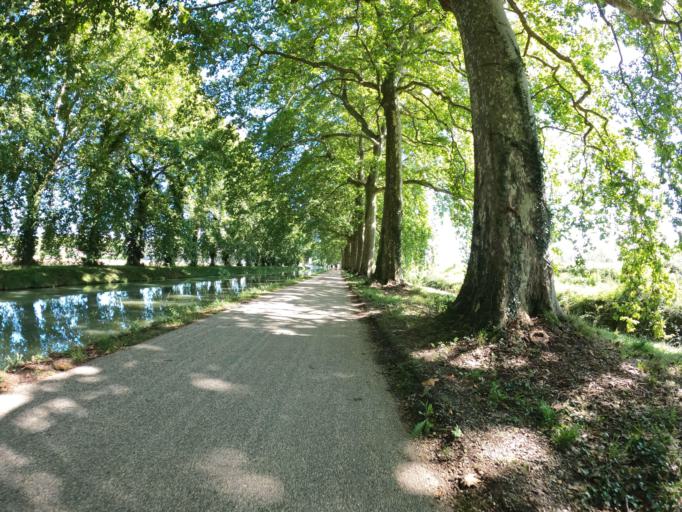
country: FR
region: Midi-Pyrenees
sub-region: Departement du Tarn-et-Garonne
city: Auvillar
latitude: 44.0907
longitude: 0.9604
